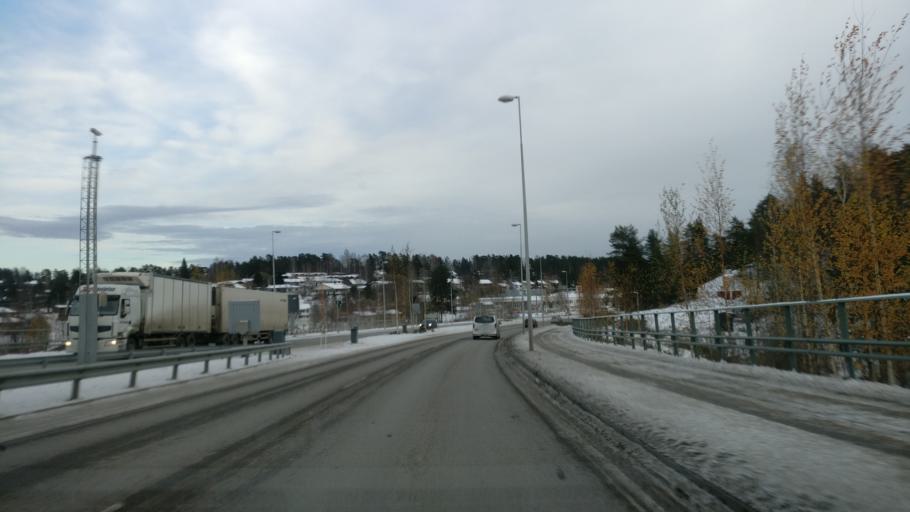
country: FI
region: Southern Savonia
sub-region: Savonlinna
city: Savonlinna
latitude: 61.8704
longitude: 28.9126
